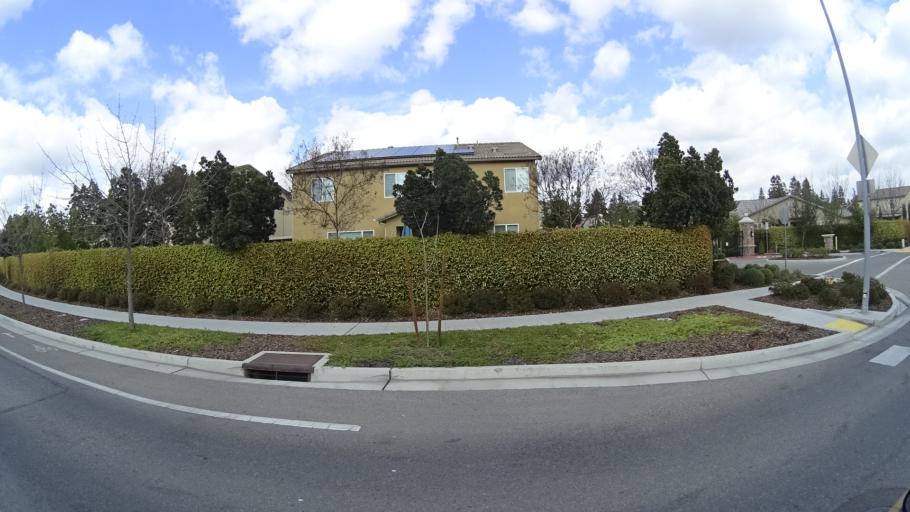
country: US
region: California
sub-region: Fresno County
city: Fresno
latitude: 36.8388
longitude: -119.8512
